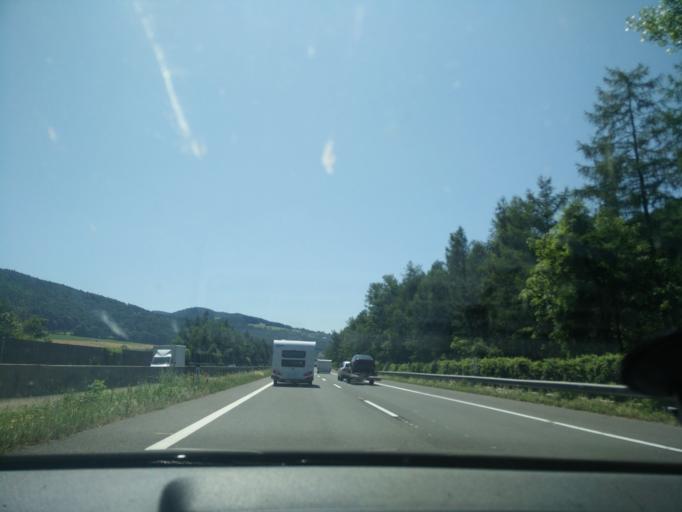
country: AT
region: Lower Austria
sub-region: Politischer Bezirk Neunkirchen
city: Warth
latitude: 47.6397
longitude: 16.1254
